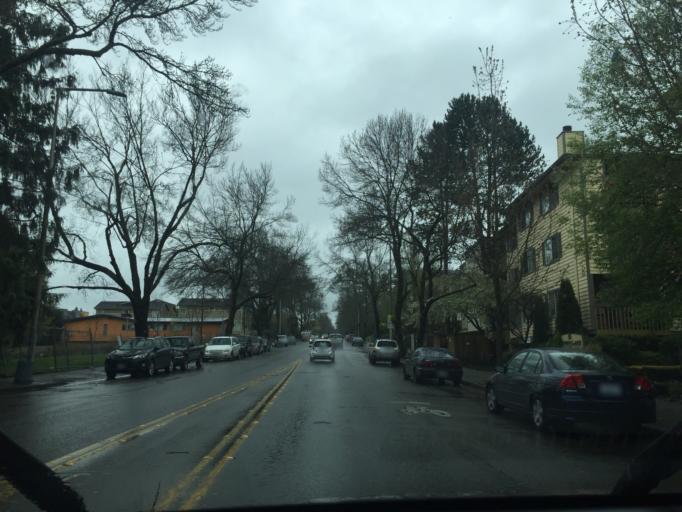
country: US
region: Washington
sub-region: King County
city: Lake Forest Park
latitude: 47.7198
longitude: -122.2908
